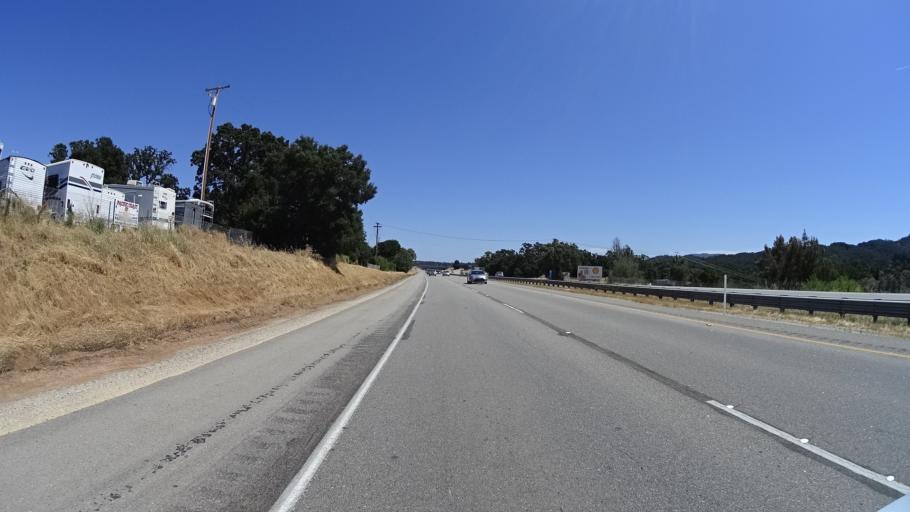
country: US
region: California
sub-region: San Luis Obispo County
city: Templeton
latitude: 35.5185
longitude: -120.7030
